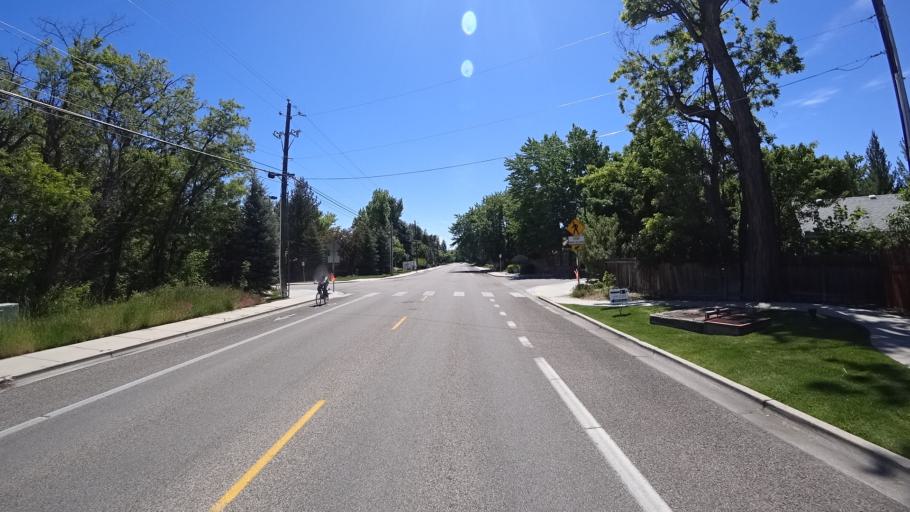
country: US
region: Idaho
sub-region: Ada County
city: Boise
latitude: 43.5679
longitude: -116.1489
